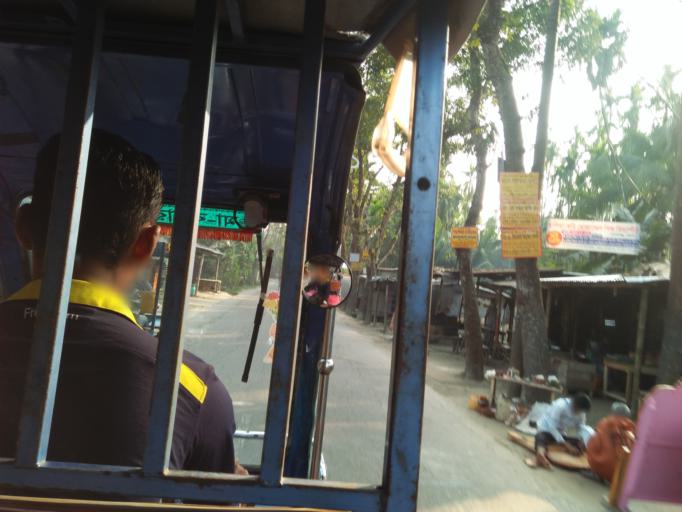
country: BD
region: Barisal
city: Bhola
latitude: 22.7071
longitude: 90.6401
